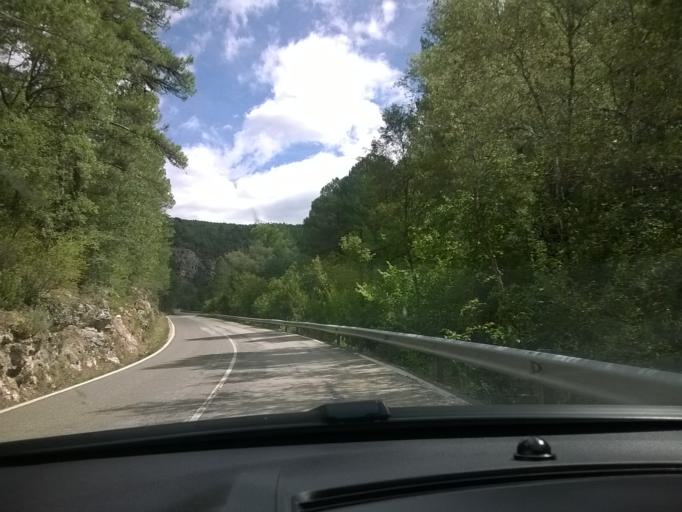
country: ES
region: Castille-La Mancha
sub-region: Provincia de Cuenca
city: Beteta
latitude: 40.5659
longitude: -2.1119
